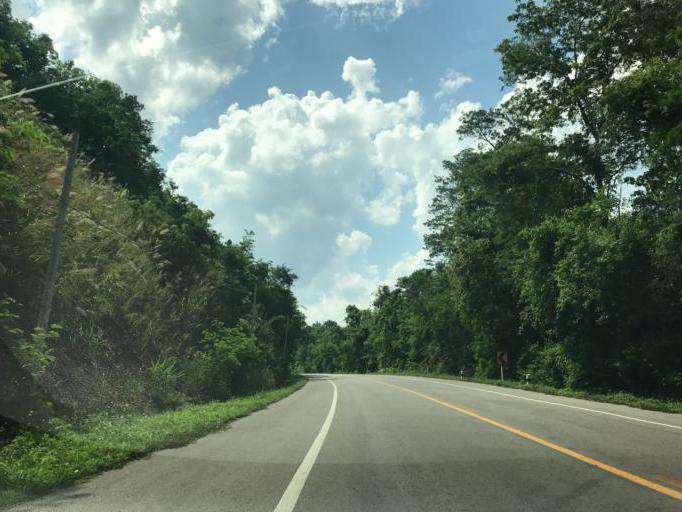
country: TH
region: Phayao
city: Phayao
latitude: 19.0868
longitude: 99.8155
